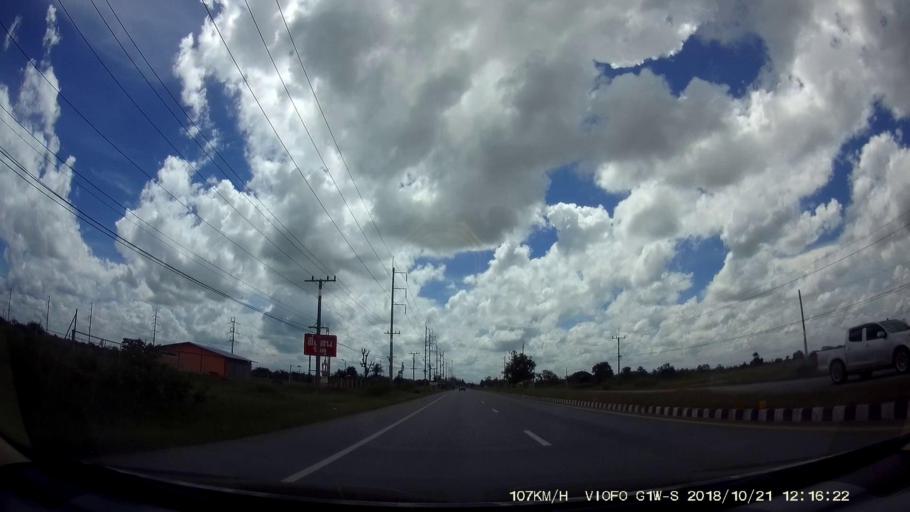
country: TH
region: Nakhon Ratchasima
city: Dan Khun Thot
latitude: 15.3485
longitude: 101.8261
